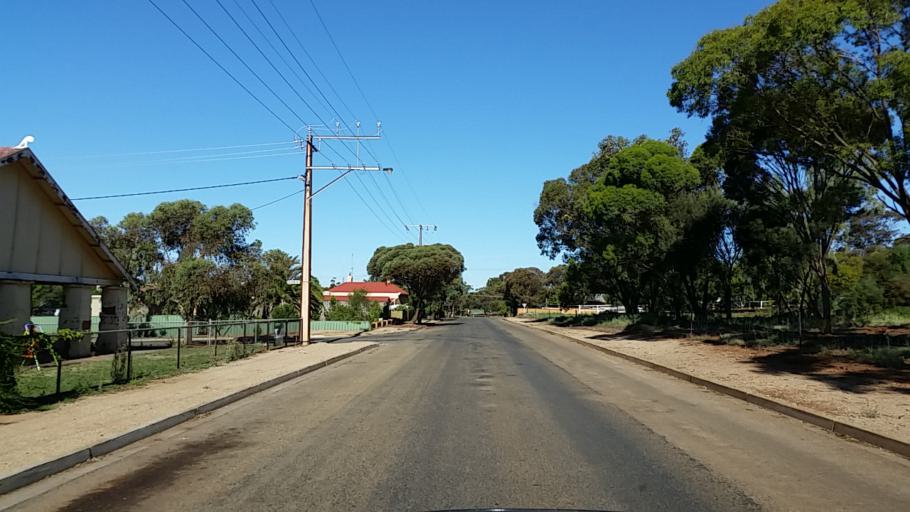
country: AU
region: South Australia
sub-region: Peterborough
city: Peterborough
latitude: -32.9796
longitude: 138.8305
